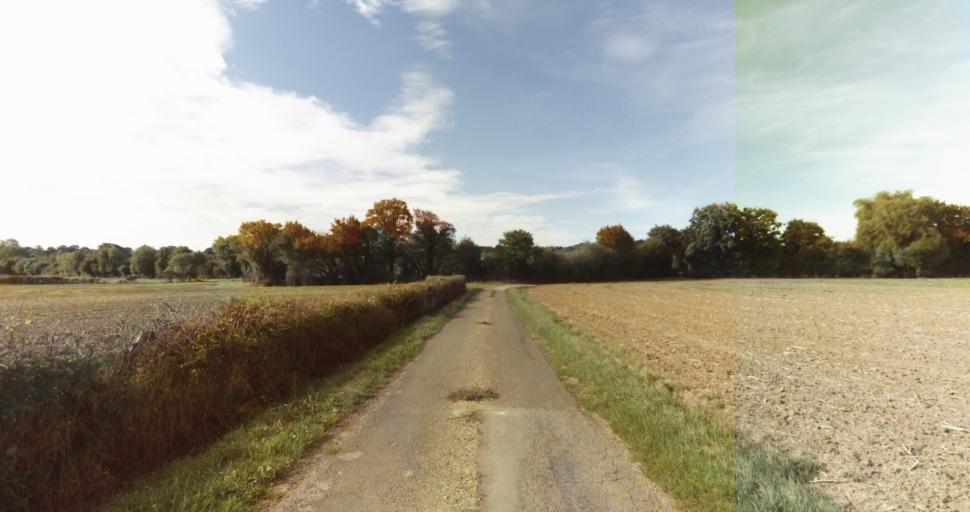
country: FR
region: Lower Normandy
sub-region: Departement de l'Orne
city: Gace
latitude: 48.7189
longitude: 0.2641
